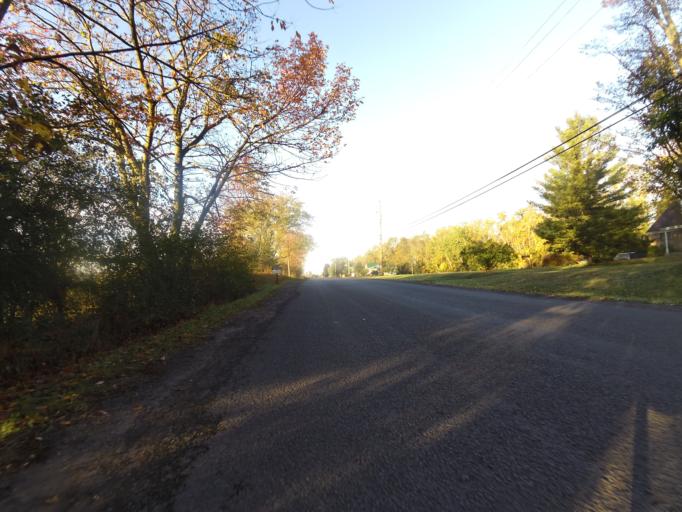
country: CA
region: Ontario
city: Quinte West
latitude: 44.0302
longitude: -77.5603
